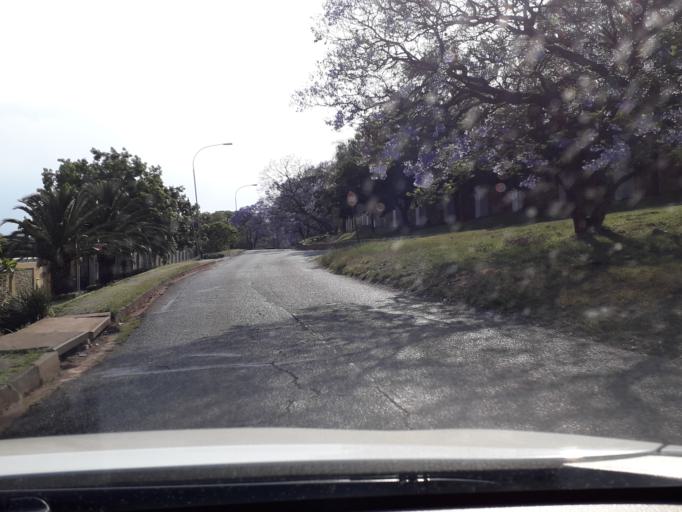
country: ZA
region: Gauteng
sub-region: City of Johannesburg Metropolitan Municipality
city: Roodepoort
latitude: -26.1412
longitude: 27.9631
